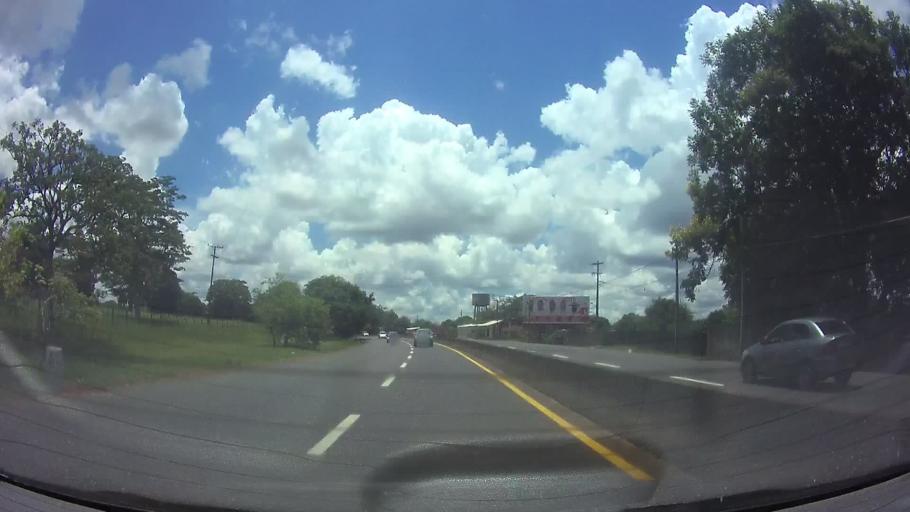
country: PY
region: Central
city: Itaugua
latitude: -25.3796
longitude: -57.3801
